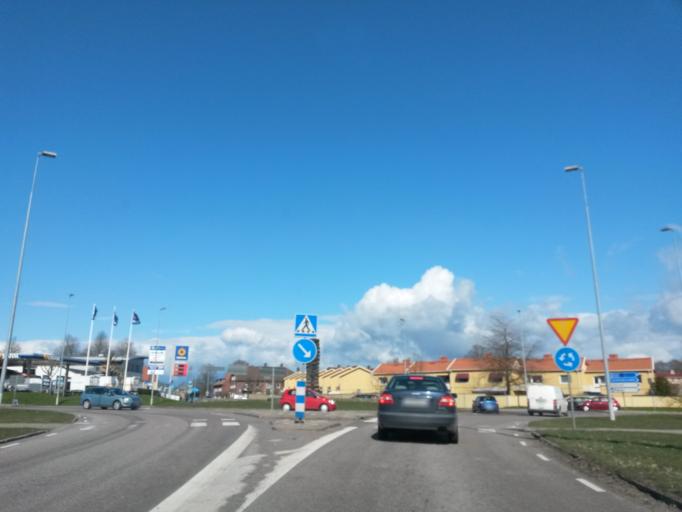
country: SE
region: Vaestra Goetaland
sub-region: Skovde Kommun
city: Skoevde
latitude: 58.3848
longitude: 13.8357
